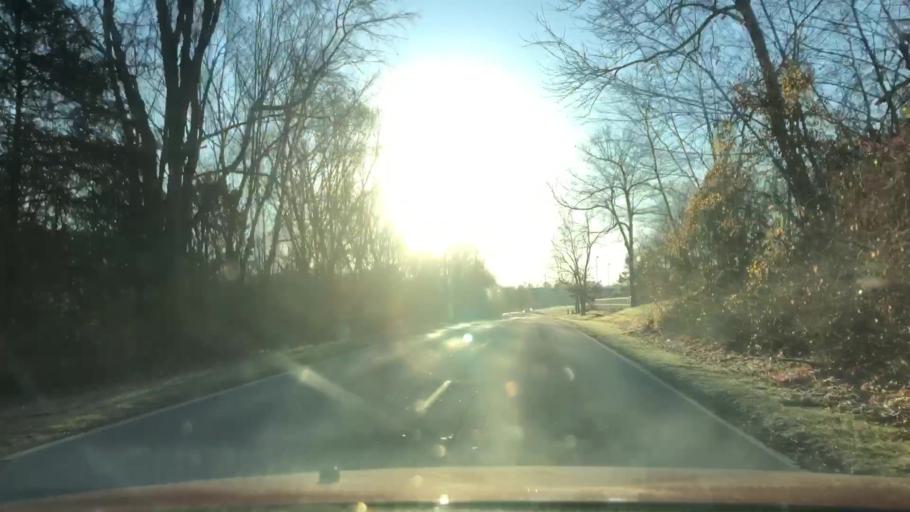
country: US
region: Missouri
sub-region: Greene County
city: Springfield
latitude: 37.1613
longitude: -93.2438
